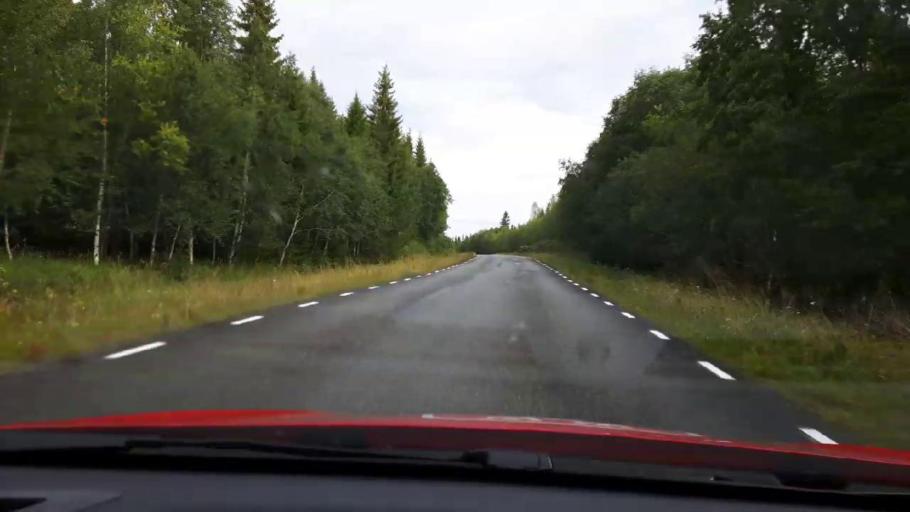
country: SE
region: Jaemtland
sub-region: Are Kommun
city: Are
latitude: 63.7290
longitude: 12.9973
